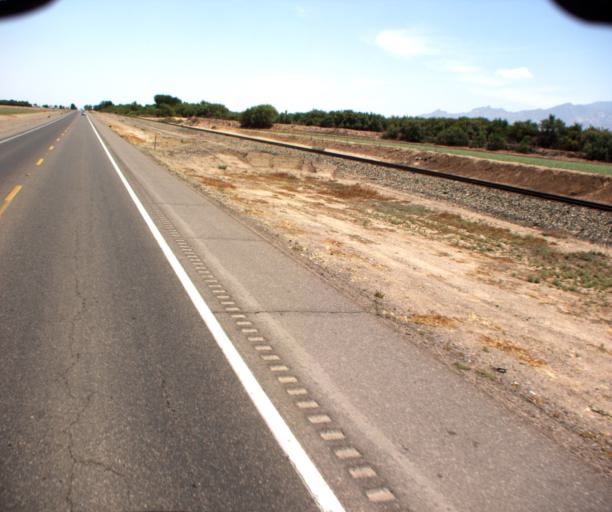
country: US
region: Arizona
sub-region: Graham County
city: Pima
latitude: 32.9082
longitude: -109.8500
